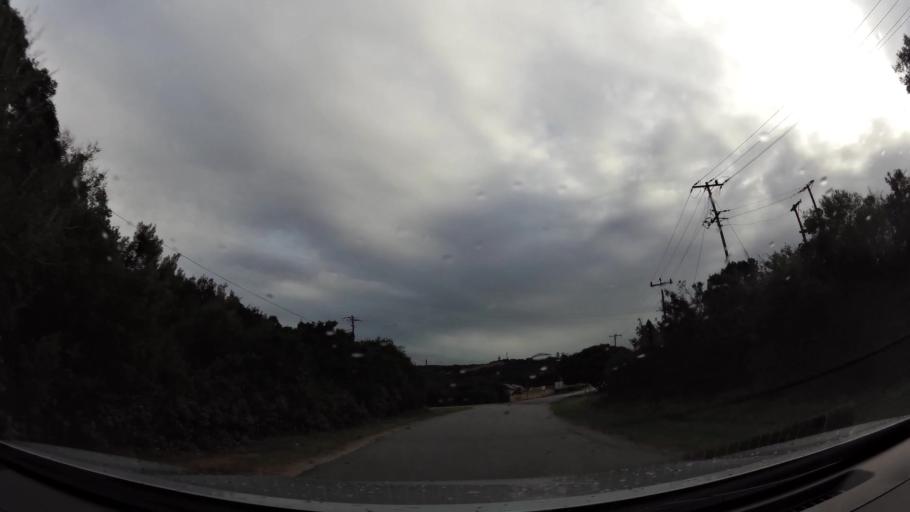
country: ZA
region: Eastern Cape
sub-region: Nelson Mandela Bay Metropolitan Municipality
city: Port Elizabeth
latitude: -34.0166
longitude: 25.4974
